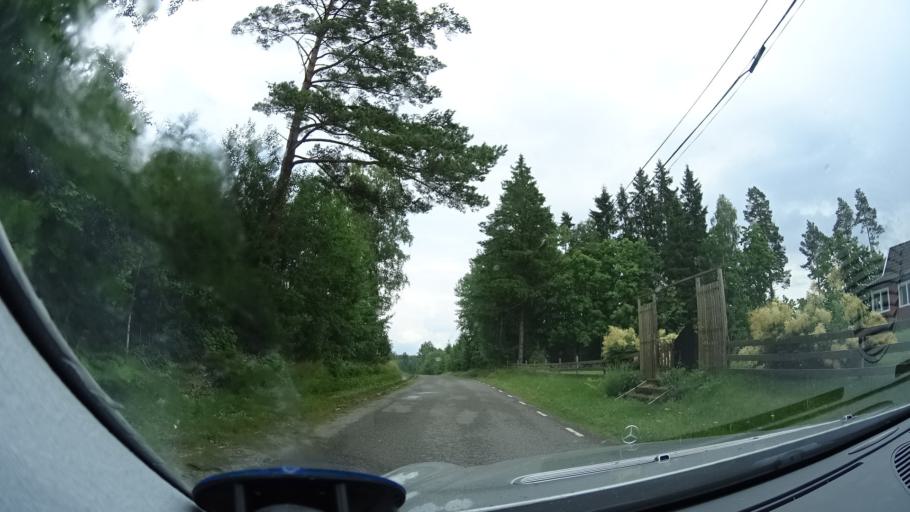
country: SE
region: Kalmar
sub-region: Emmaboda Kommun
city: Emmaboda
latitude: 56.6561
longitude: 15.7293
